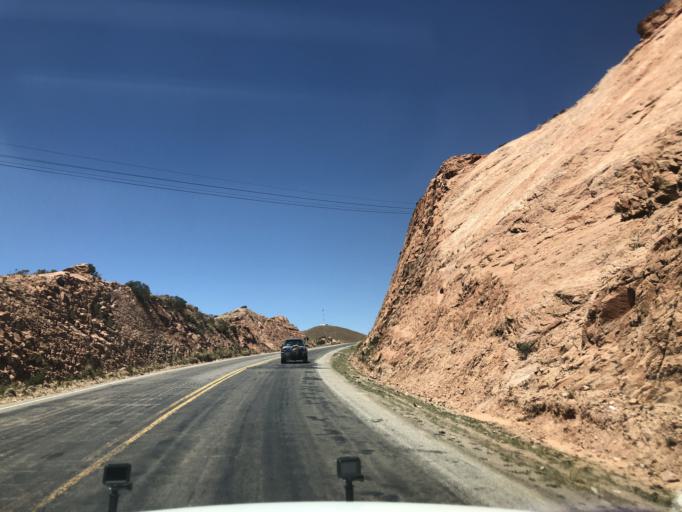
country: BO
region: Cochabamba
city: Colchani
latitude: -17.6895
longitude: -66.7071
